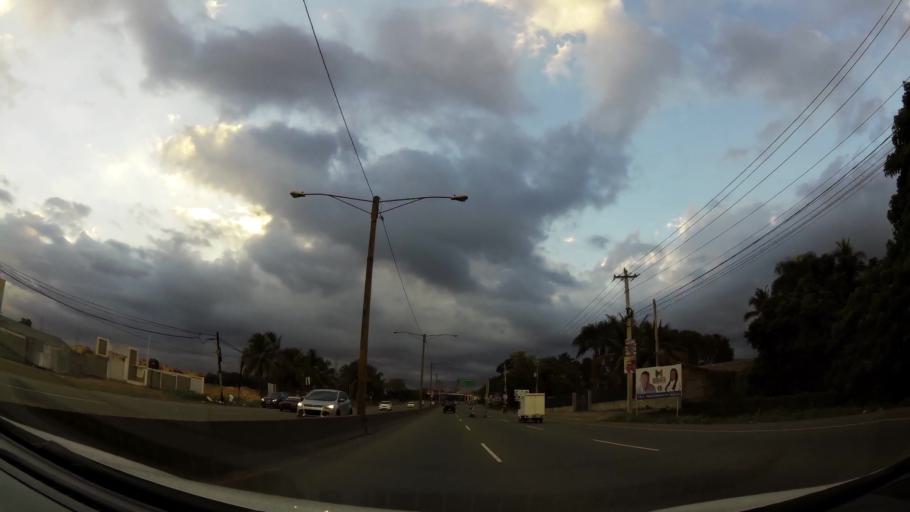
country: DO
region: Santo Domingo
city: Santo Domingo Oeste
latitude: 18.5397
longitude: -70.0300
